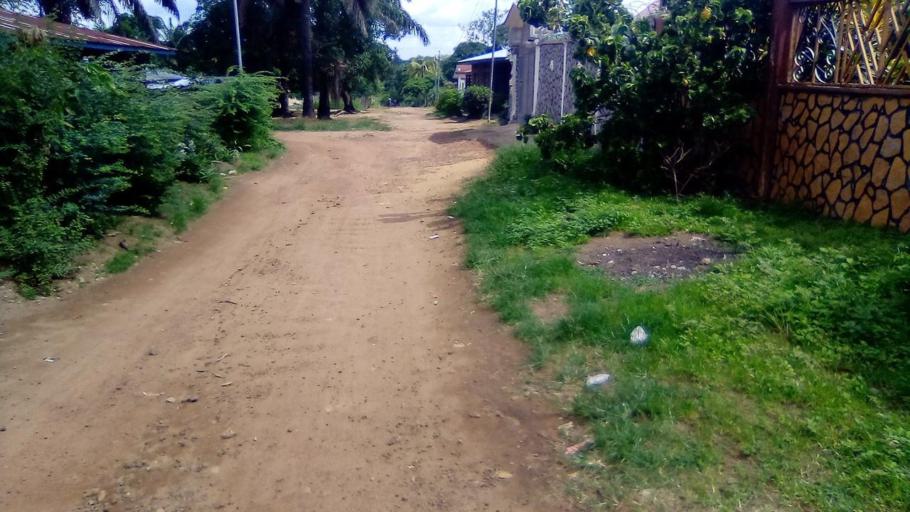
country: SL
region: Southern Province
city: Bo
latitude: 7.9603
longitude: -11.7214
